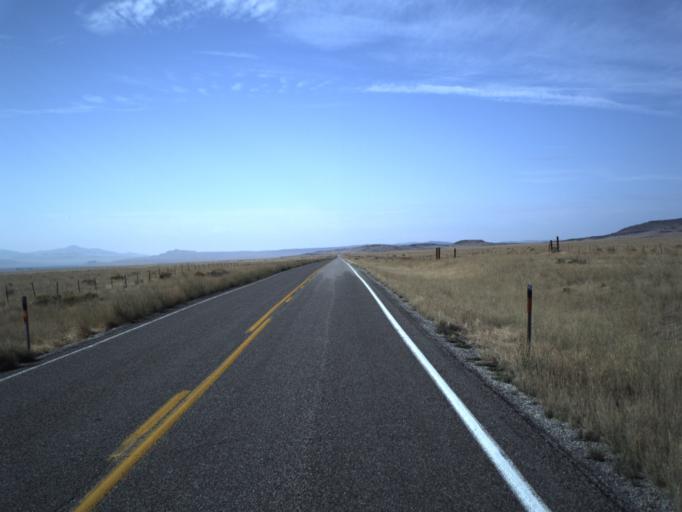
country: US
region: Idaho
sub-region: Oneida County
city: Malad City
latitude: 41.8839
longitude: -113.1157
